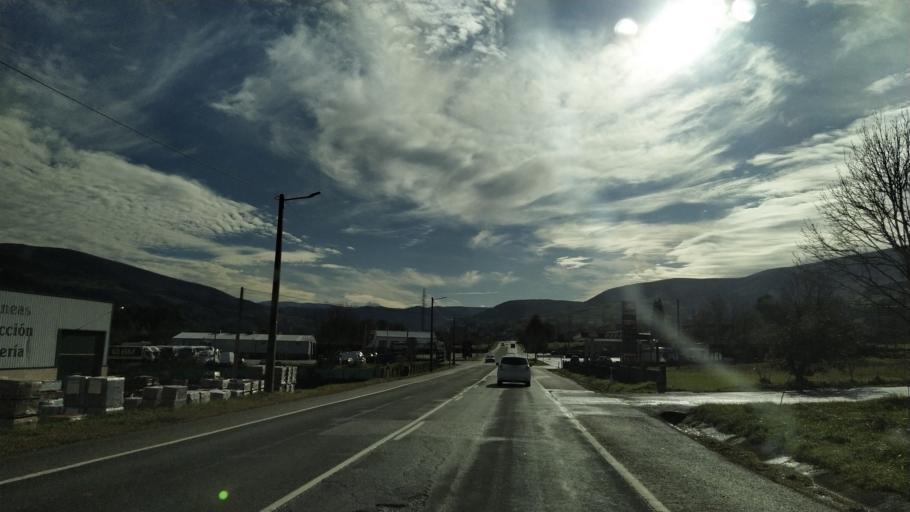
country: ES
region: Cantabria
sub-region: Provincia de Cantabria
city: Santiurde de Toranzo
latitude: 43.2207
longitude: -3.9447
